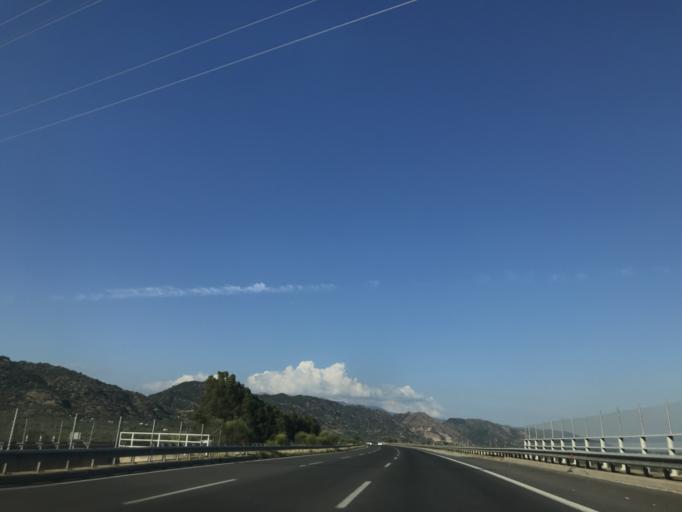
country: TR
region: Aydin
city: Germencik
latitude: 37.8700
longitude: 27.6623
